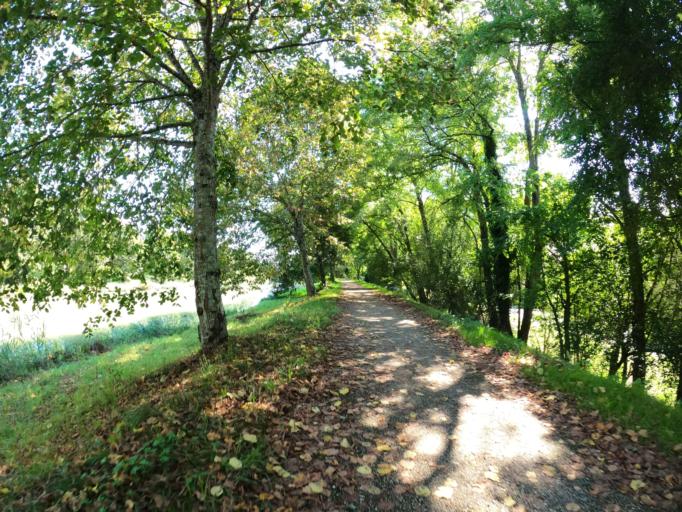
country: FR
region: Midi-Pyrenees
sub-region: Departement du Tarn-et-Garonne
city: Lamagistere
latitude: 44.1345
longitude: 0.8189
